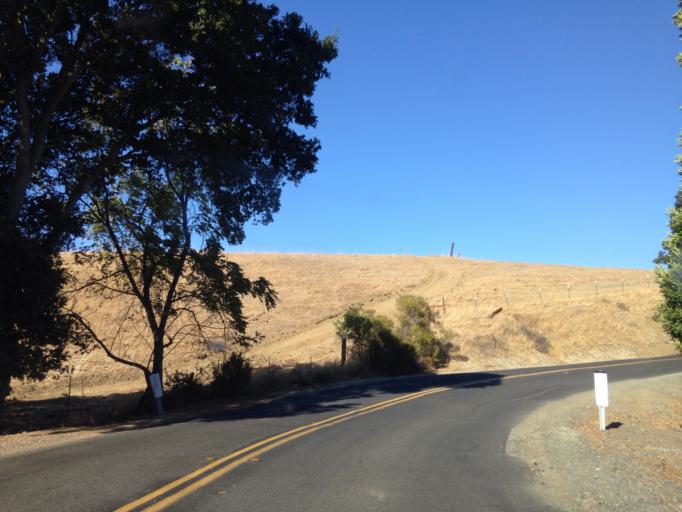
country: US
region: California
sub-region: Contra Costa County
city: Crockett
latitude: 38.0466
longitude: -122.1977
